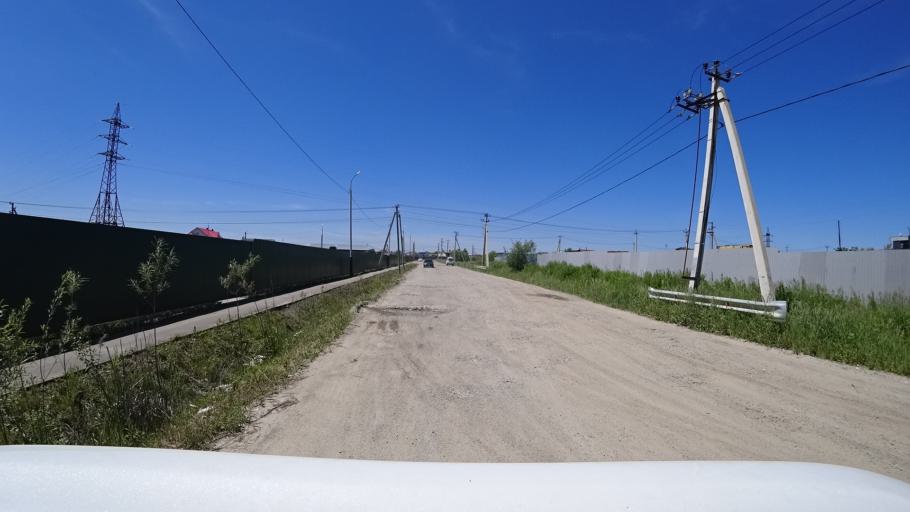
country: RU
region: Khabarovsk Krai
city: Topolevo
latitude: 48.5018
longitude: 135.1856
